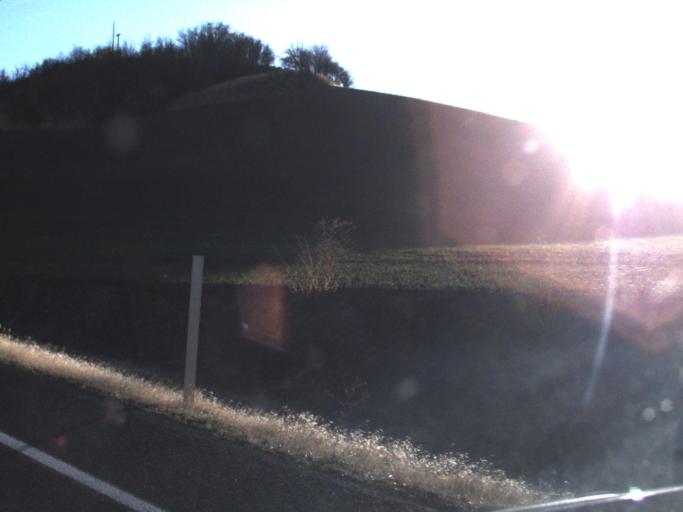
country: US
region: Washington
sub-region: Walla Walla County
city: Waitsburg
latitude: 46.1885
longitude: -118.1374
